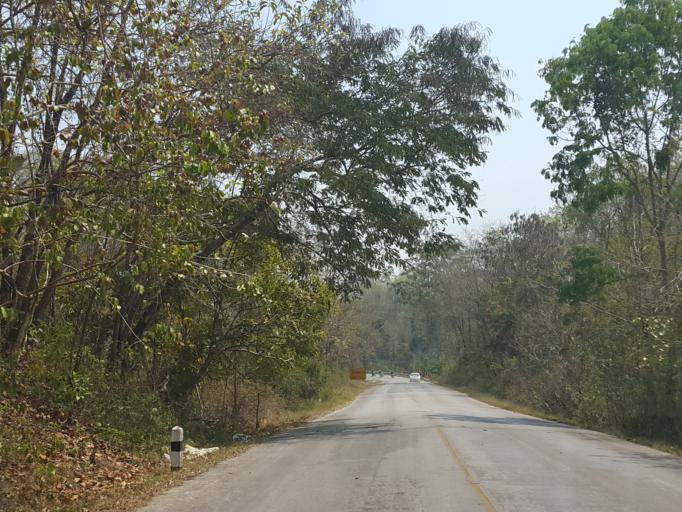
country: TH
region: Lampang
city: Mueang Pan
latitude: 18.7762
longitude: 99.5432
